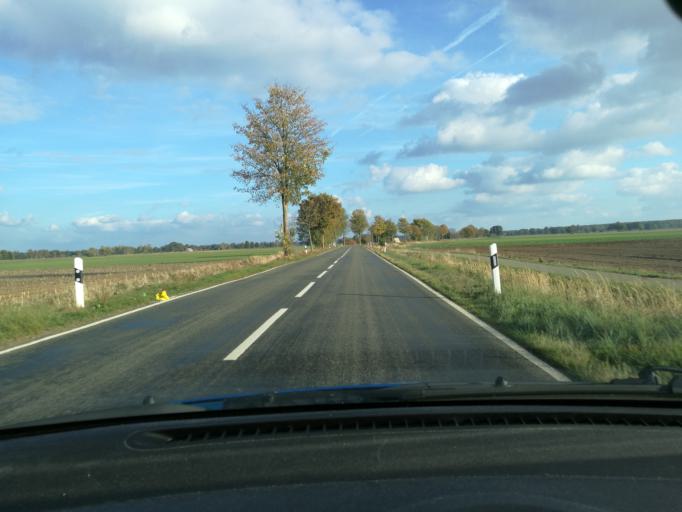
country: DE
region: Lower Saxony
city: Prezelle
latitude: 52.9063
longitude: 11.4124
